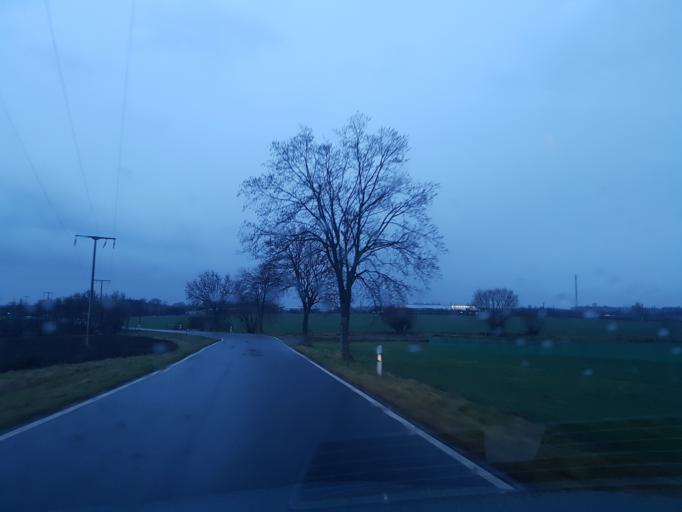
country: DE
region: Saxony
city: Priestewitz
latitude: 51.2502
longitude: 13.5204
